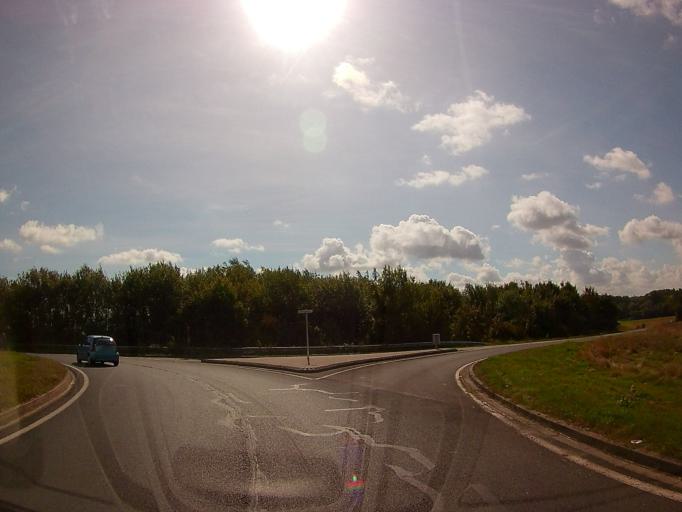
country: FR
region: Picardie
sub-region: Departement de la Somme
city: Peronne
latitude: 49.9599
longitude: 2.8608
